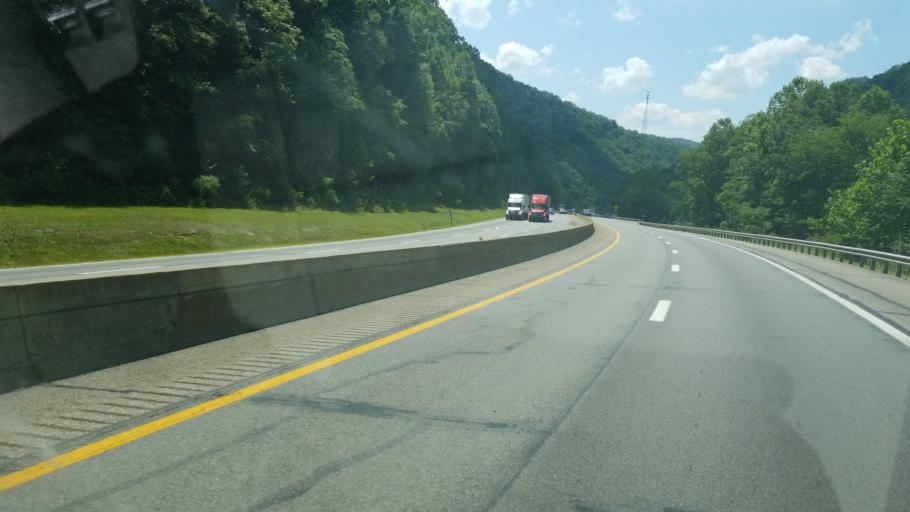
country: US
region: West Virginia
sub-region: Kanawha County
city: Montgomery
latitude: 38.1339
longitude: -81.4280
